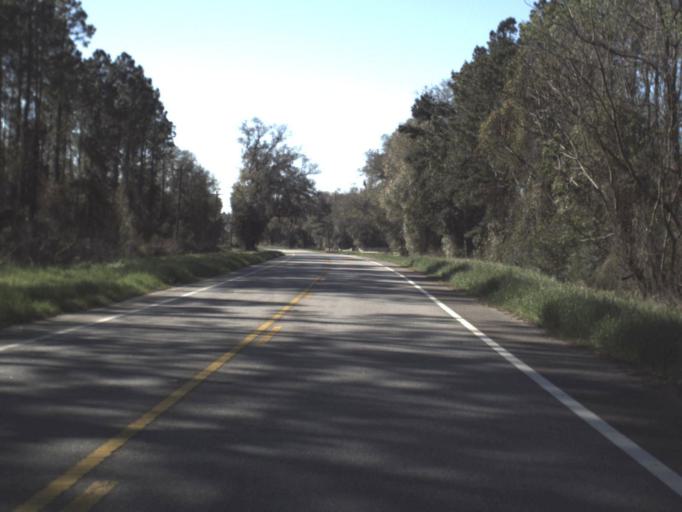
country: US
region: Georgia
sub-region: Brooks County
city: Quitman
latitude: 30.6088
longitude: -83.6463
